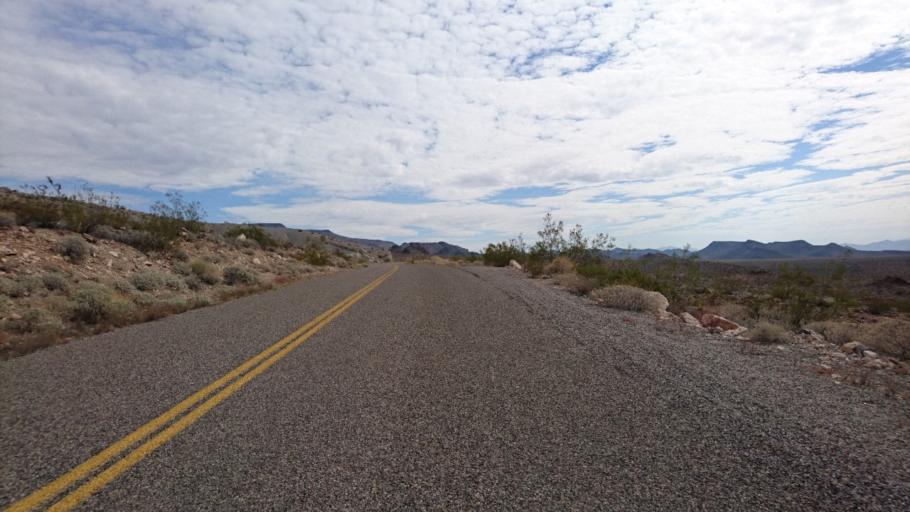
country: US
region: Arizona
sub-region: Mohave County
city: Mohave Valley
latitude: 34.9801
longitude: -114.4232
